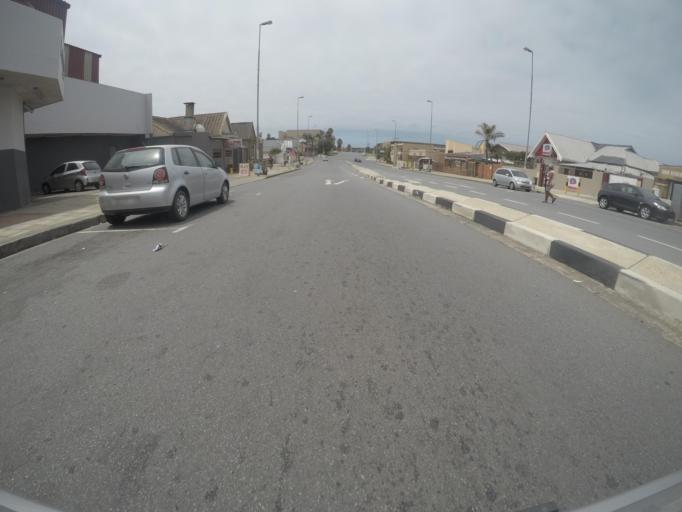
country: ZA
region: Eastern Cape
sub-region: Buffalo City Metropolitan Municipality
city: East London
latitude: -33.0170
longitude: 27.9152
